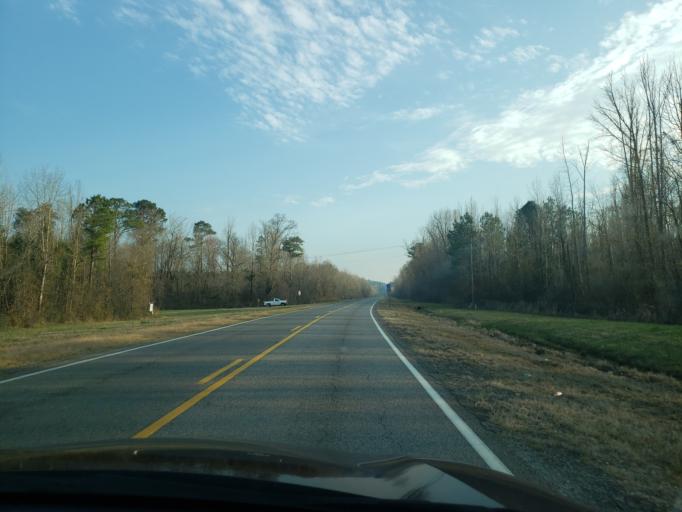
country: US
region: Alabama
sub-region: Hale County
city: Greensboro
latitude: 32.7734
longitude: -87.5856
